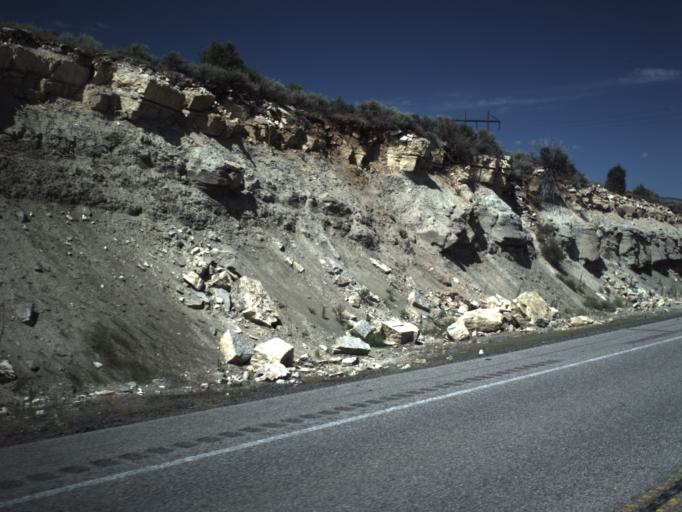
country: US
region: Utah
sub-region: Carbon County
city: Helper
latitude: 39.8225
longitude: -110.9453
